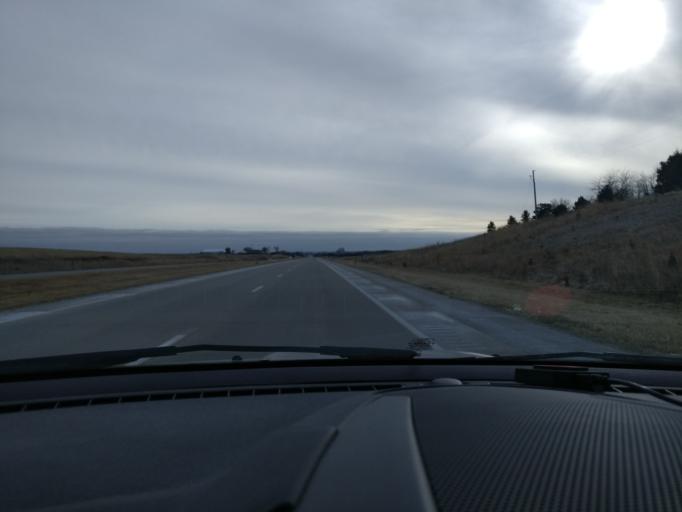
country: US
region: Nebraska
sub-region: Saunders County
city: Wahoo
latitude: 41.0859
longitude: -96.6402
